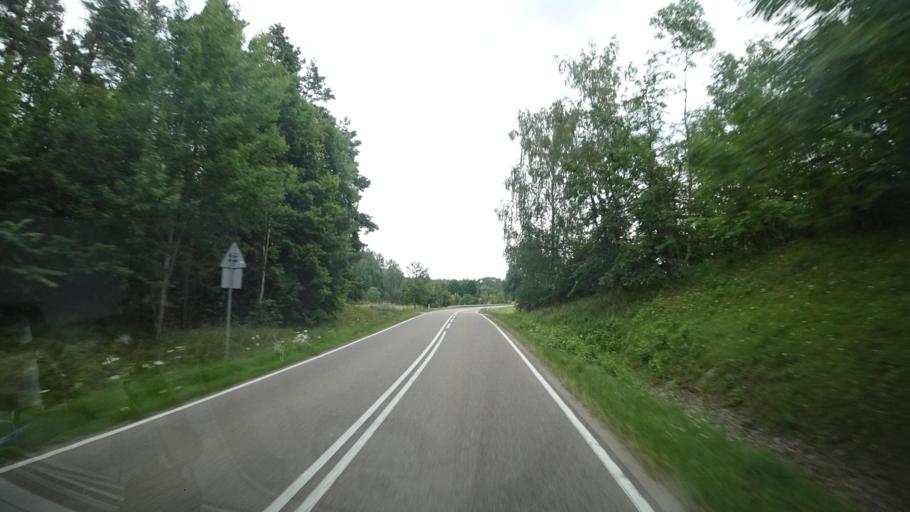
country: PL
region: Warmian-Masurian Voivodeship
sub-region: Powiat piski
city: Orzysz
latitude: 53.8247
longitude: 21.7994
